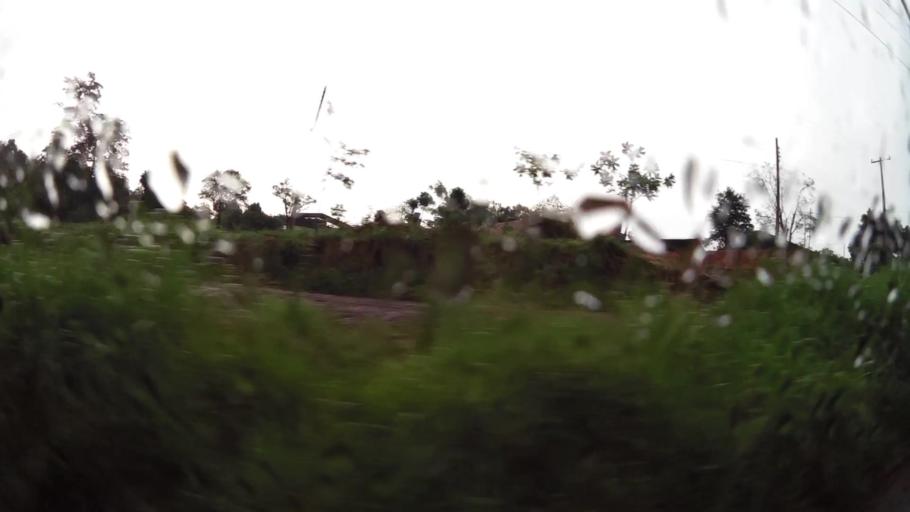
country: PY
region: Alto Parana
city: Presidente Franco
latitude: -25.5218
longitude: -54.6761
